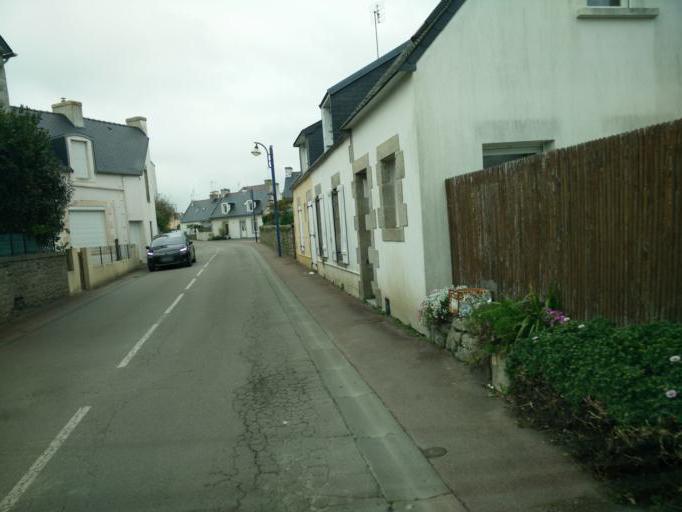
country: FR
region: Brittany
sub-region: Departement du Finistere
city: Plobannalec-Lesconil
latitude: 47.7992
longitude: -4.2196
